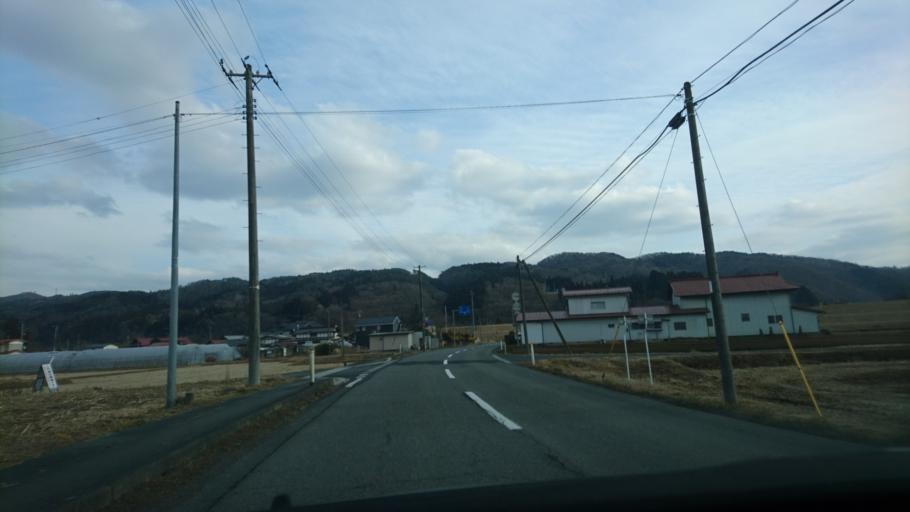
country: JP
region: Iwate
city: Ichinoseki
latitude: 38.8313
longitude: 141.2522
